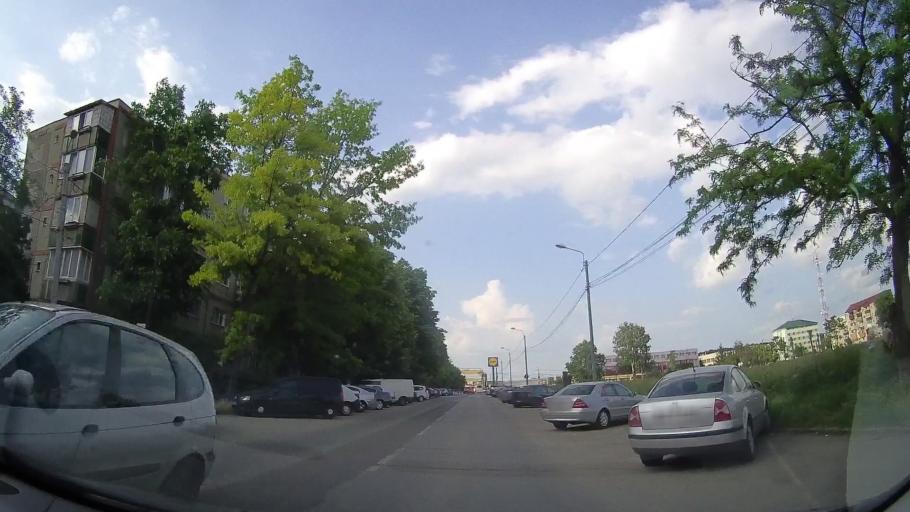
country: RO
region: Timis
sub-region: Comuna Dumbravita
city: Dumbravita
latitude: 45.7769
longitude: 21.2403
